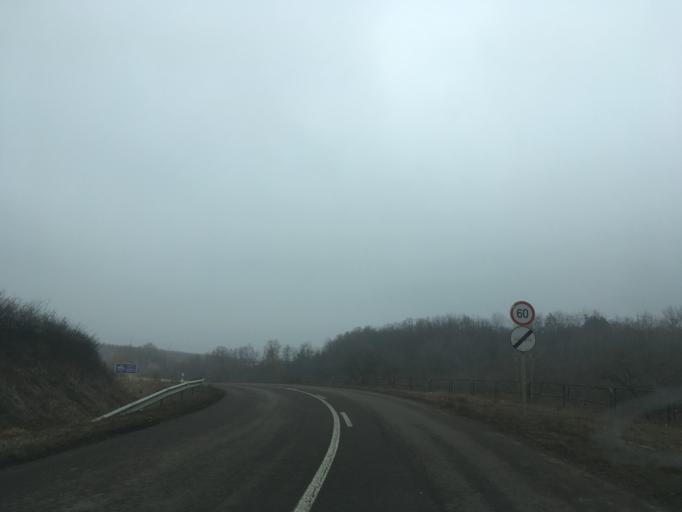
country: HU
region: Heves
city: Eger
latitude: 47.8663
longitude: 20.3740
